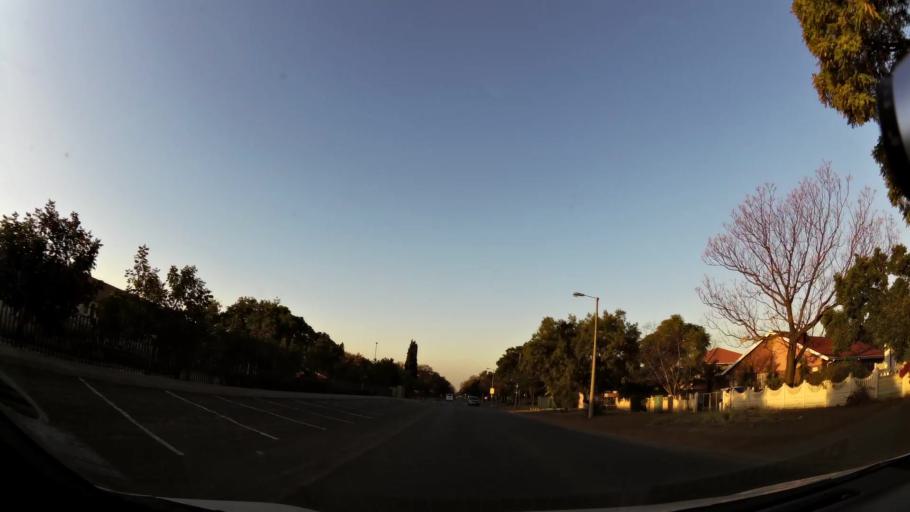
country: ZA
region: North-West
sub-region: Bojanala Platinum District Municipality
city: Rustenburg
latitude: -25.6746
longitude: 27.2240
